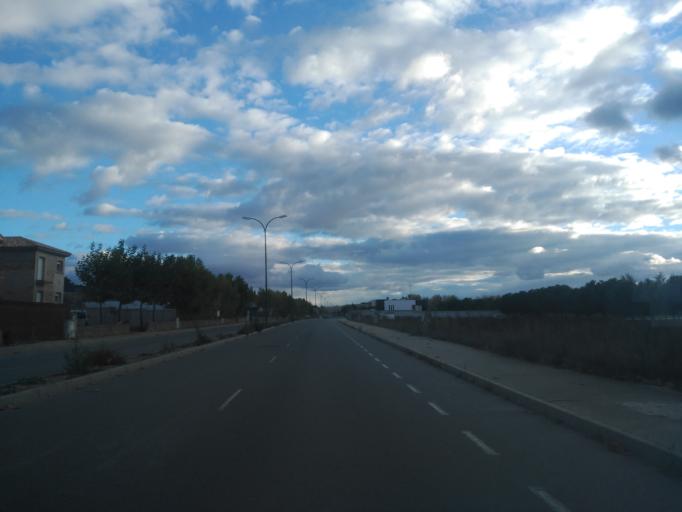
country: ES
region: Castille and Leon
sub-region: Provincia de Salamanca
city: Villamayor
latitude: 40.9884
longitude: -5.7141
